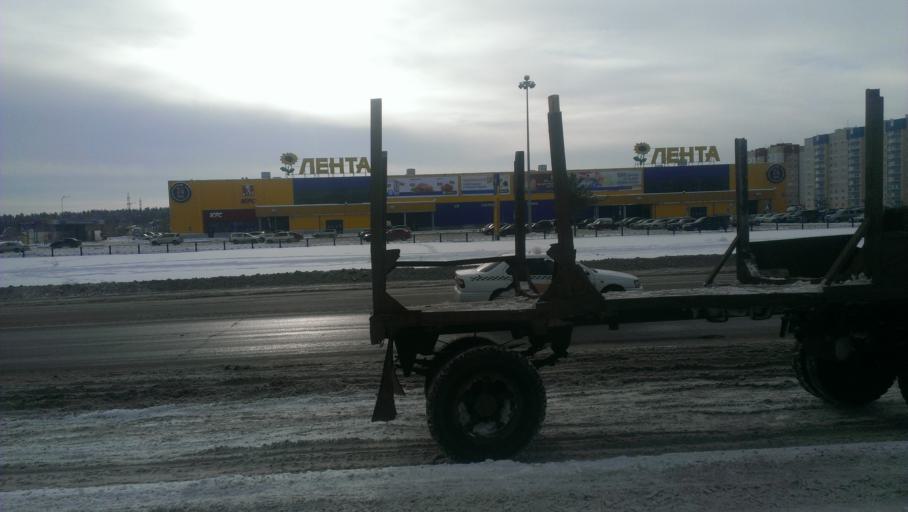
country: RU
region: Altai Krai
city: Novosilikatnyy
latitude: 53.3281
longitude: 83.6857
